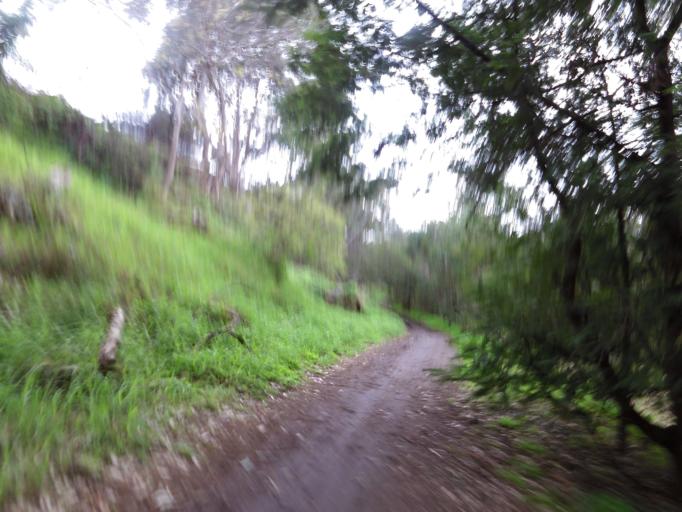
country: AU
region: Victoria
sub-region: Yarra
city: Richmond
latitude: -37.8097
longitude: 145.0088
